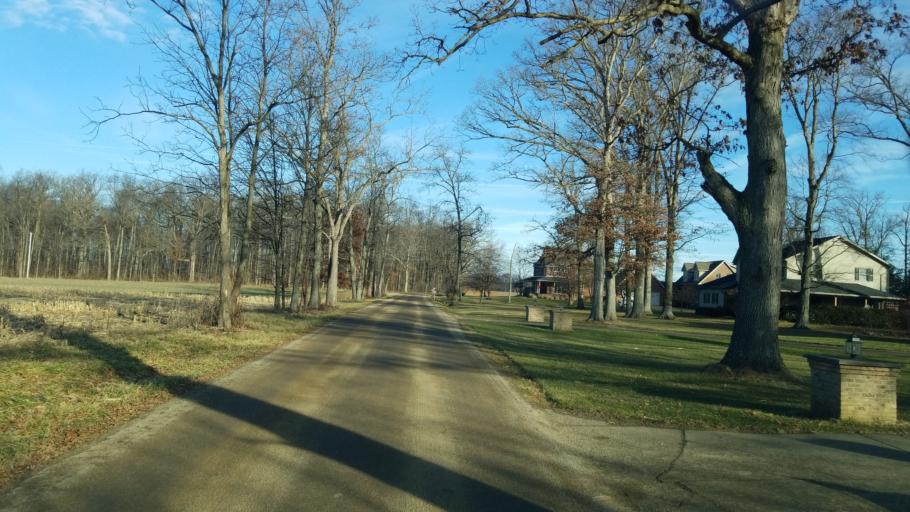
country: US
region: Ohio
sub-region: Knox County
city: Gambier
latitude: 40.3599
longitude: -82.4329
